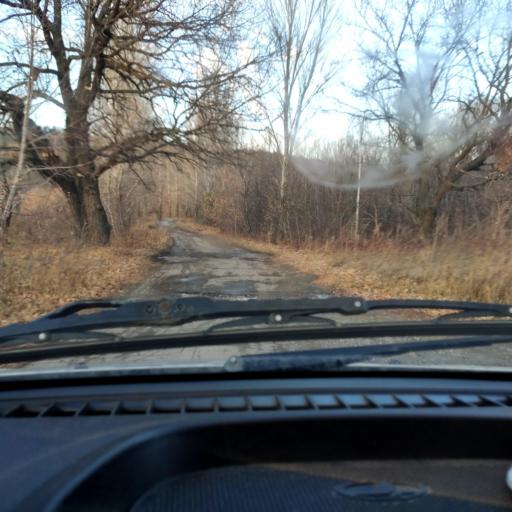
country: RU
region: Samara
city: Povolzhskiy
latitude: 53.4663
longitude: 49.6859
